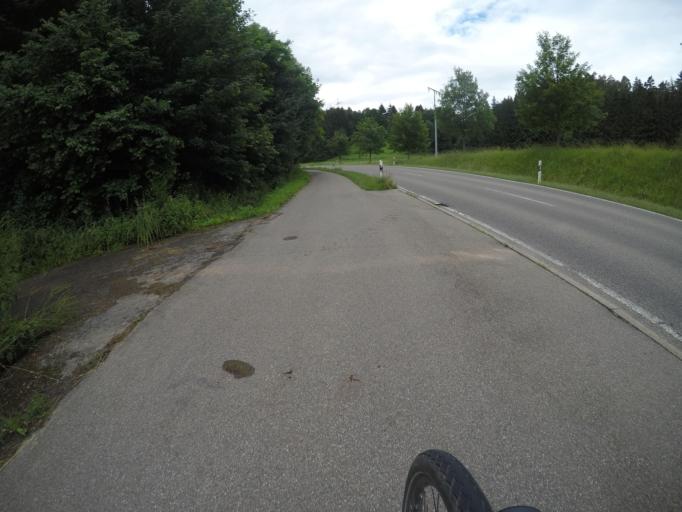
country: DE
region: Baden-Wuerttemberg
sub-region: Regierungsbezirk Stuttgart
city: Gartringen
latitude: 48.6539
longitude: 8.8823
